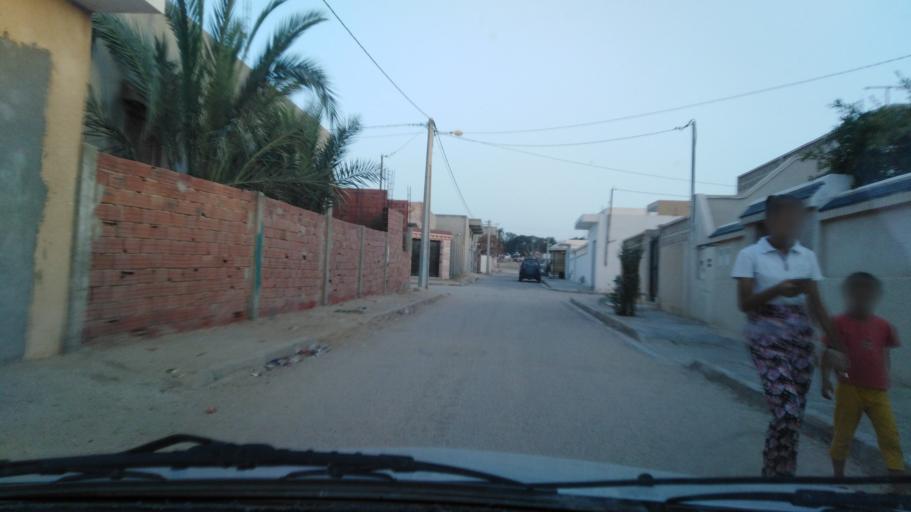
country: TN
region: Qabis
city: Gabes
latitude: 33.9542
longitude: 9.9976
